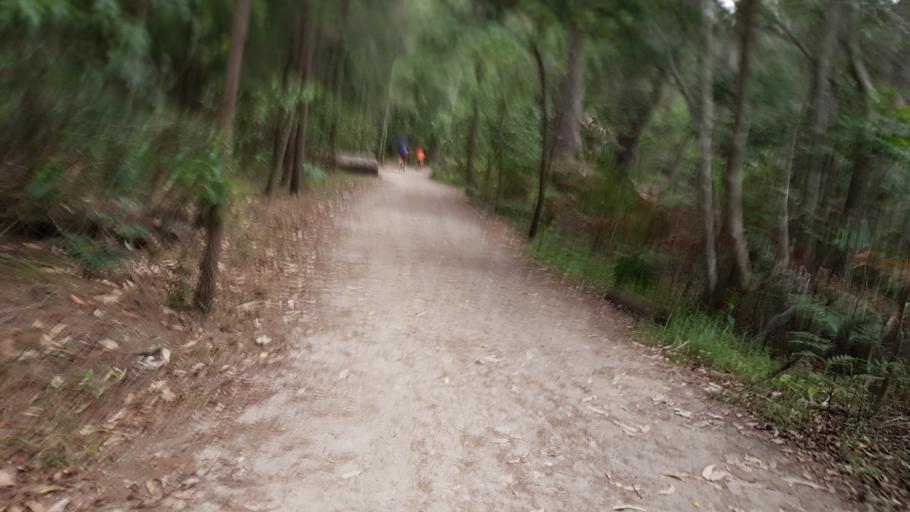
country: AU
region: New South Wales
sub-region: Pittwater
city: North Narrabeen
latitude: -33.7167
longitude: 151.2811
